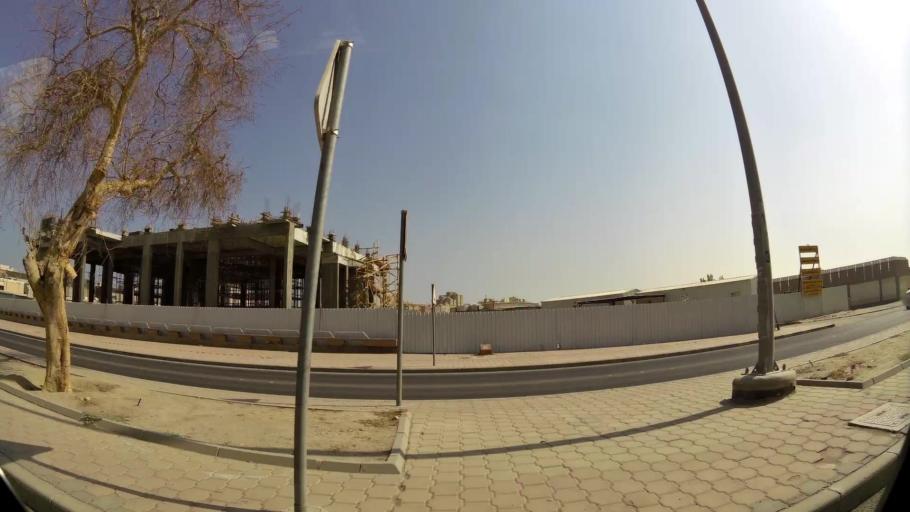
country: KW
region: Al Ahmadi
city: Al Fahahil
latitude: 29.0855
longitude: 48.1191
